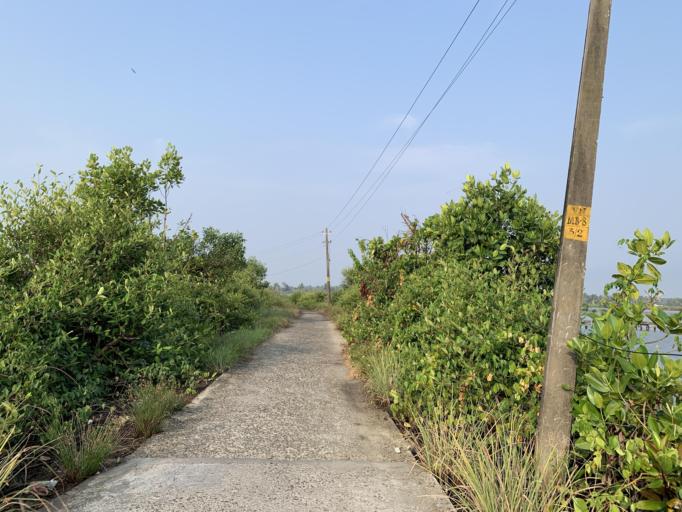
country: IN
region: Kerala
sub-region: Ernakulam
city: Elur
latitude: 10.0196
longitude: 76.2232
